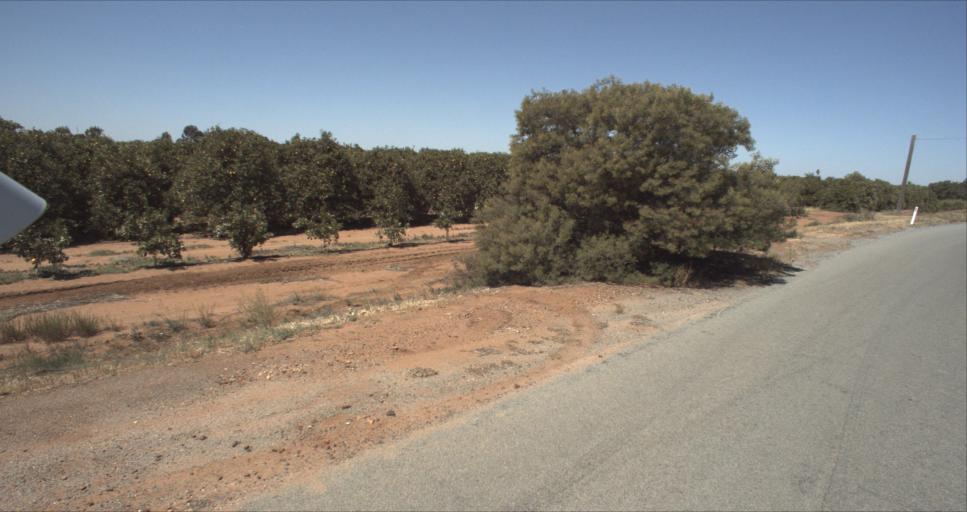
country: AU
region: New South Wales
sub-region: Leeton
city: Leeton
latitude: -34.5338
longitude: 146.3989
